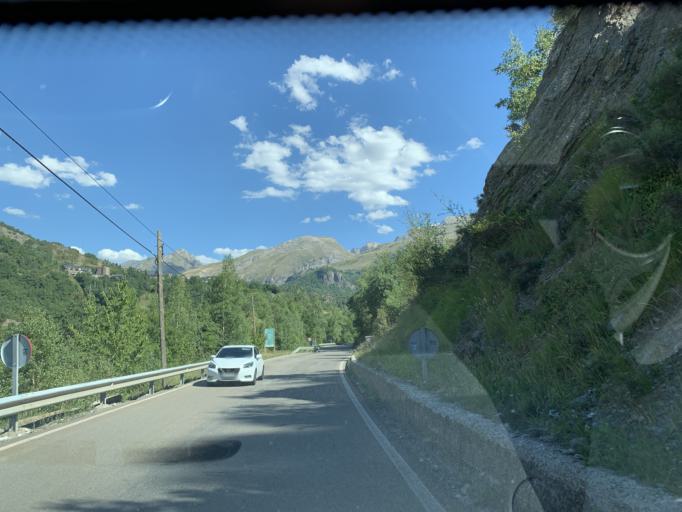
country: ES
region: Aragon
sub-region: Provincia de Huesca
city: Hoz de Jaca
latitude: 42.7285
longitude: -0.3088
